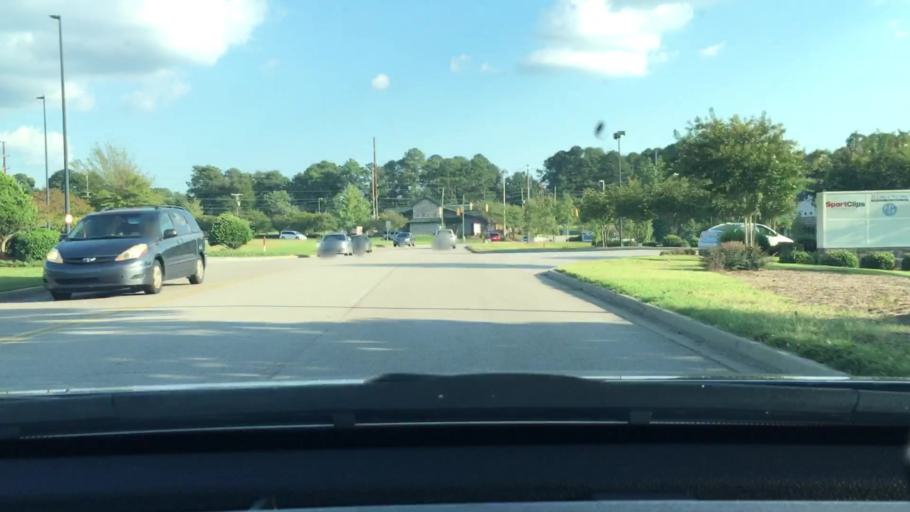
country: US
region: South Carolina
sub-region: Lexington County
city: Seven Oaks
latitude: 34.0720
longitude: -81.1530
